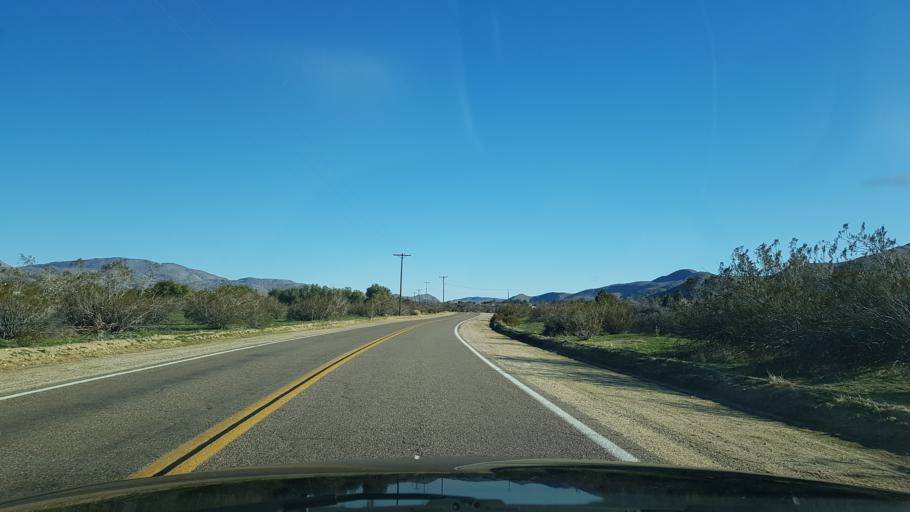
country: US
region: California
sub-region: San Diego County
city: Julian
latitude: 33.0882
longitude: -116.4499
